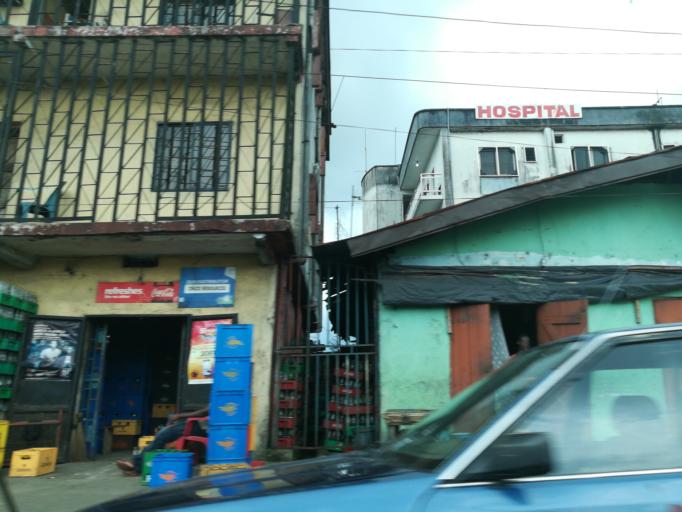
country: NG
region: Rivers
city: Port Harcourt
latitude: 4.7977
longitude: 6.9921
